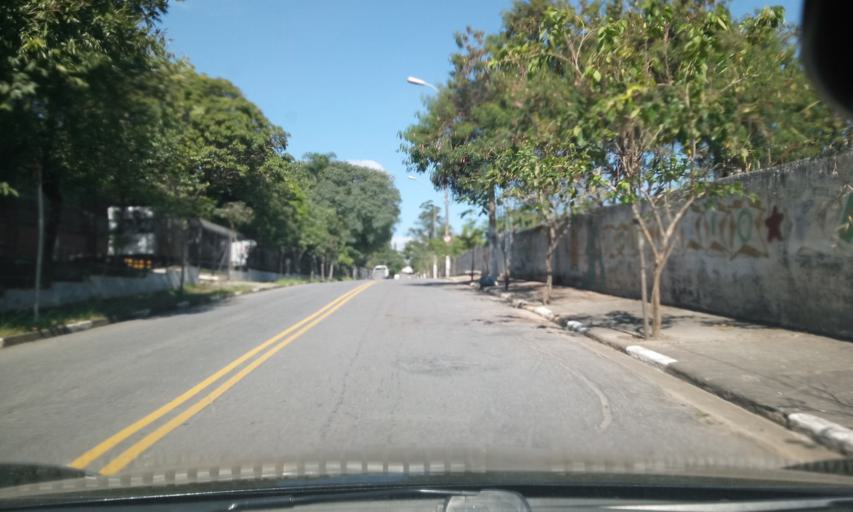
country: BR
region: Sao Paulo
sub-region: Sao Bernardo Do Campo
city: Sao Bernardo do Campo
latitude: -23.7123
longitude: -46.5776
